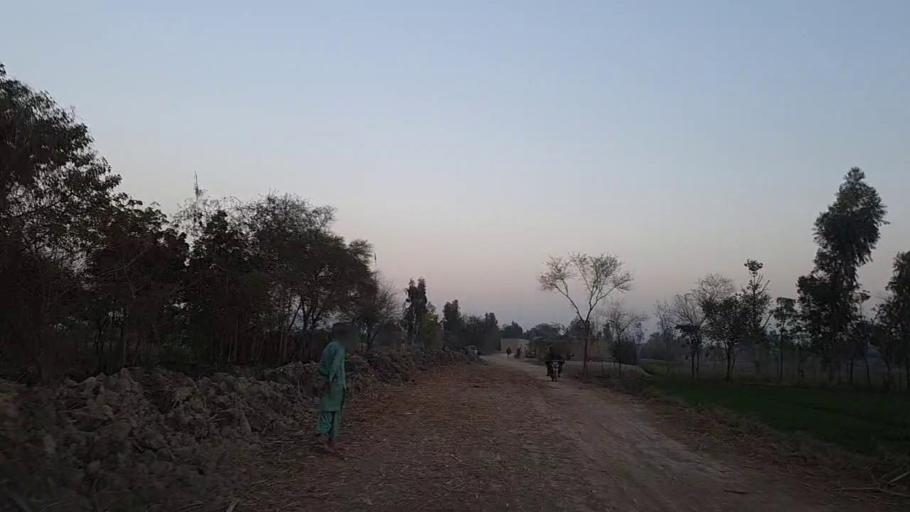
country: PK
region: Sindh
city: Naushahro Firoz
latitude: 26.7989
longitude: 68.0326
